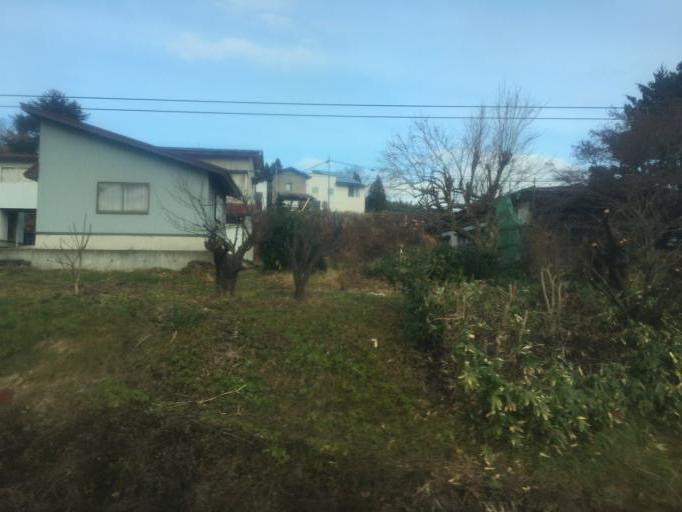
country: JP
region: Akita
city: Takanosu
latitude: 40.2639
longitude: 140.4188
